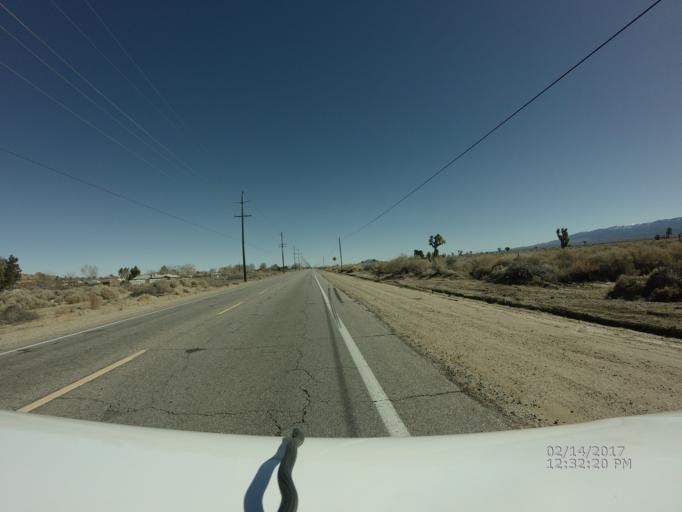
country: US
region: California
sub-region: Los Angeles County
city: Lake Los Angeles
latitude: 34.5799
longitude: -117.8596
